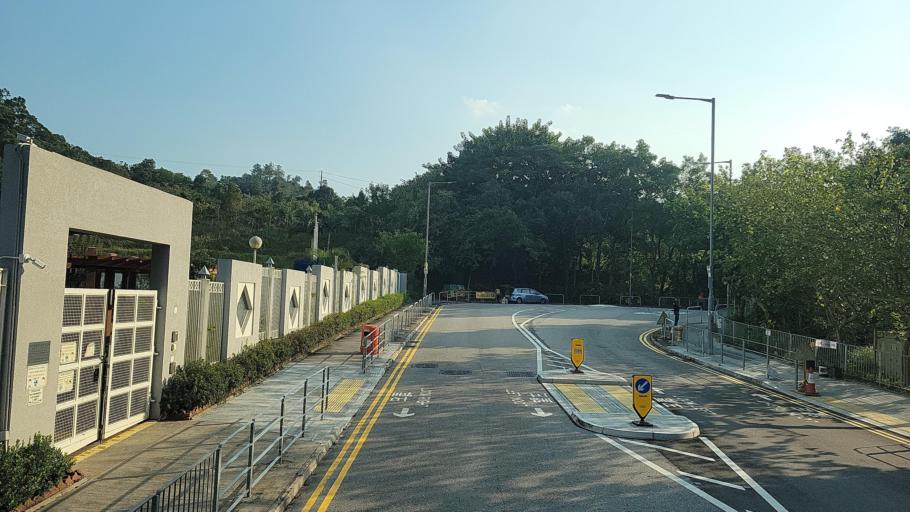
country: HK
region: Tuen Mun
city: Tuen Mun
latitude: 22.3720
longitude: 114.0035
